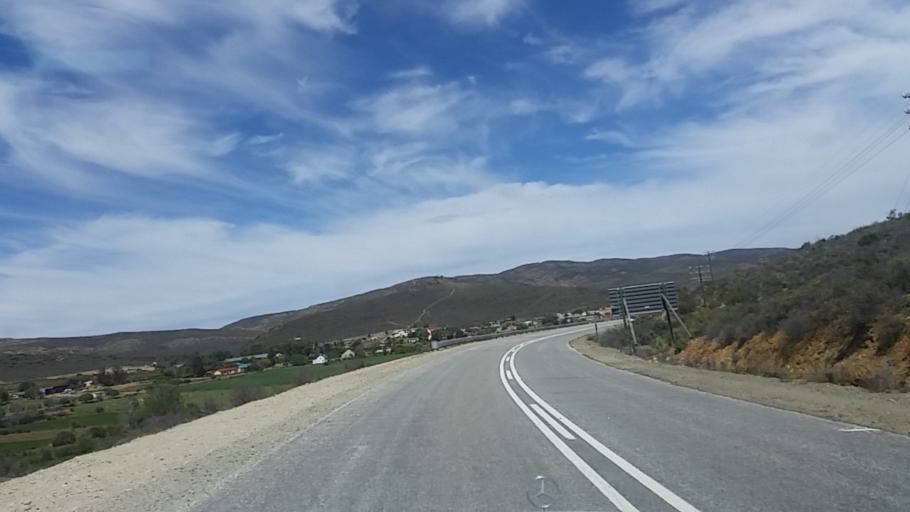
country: ZA
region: Western Cape
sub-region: Eden District Municipality
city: Knysna
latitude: -33.6445
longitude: 23.1332
